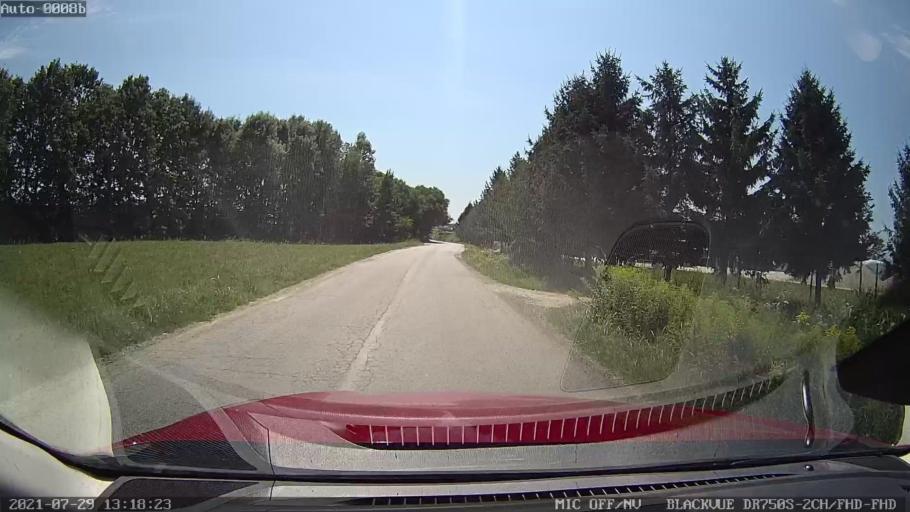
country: HR
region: Varazdinska
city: Varazdin
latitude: 46.2703
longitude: 16.3813
